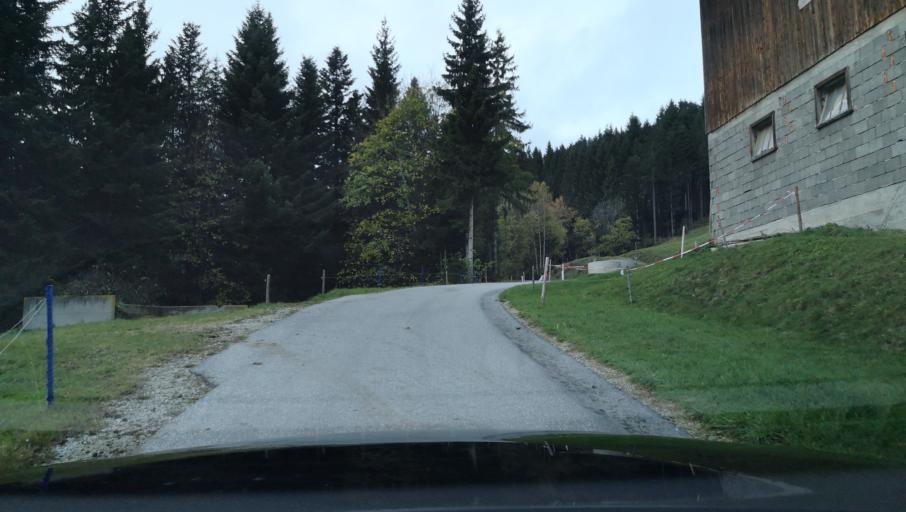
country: AT
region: Styria
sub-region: Politischer Bezirk Weiz
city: Gasen
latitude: 47.3580
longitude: 15.6088
